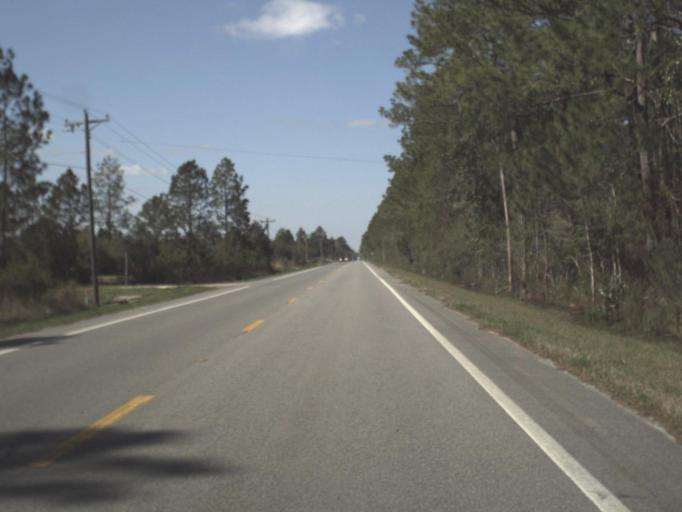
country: US
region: Florida
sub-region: Gulf County
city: Wewahitchka
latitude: 30.0277
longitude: -85.1806
